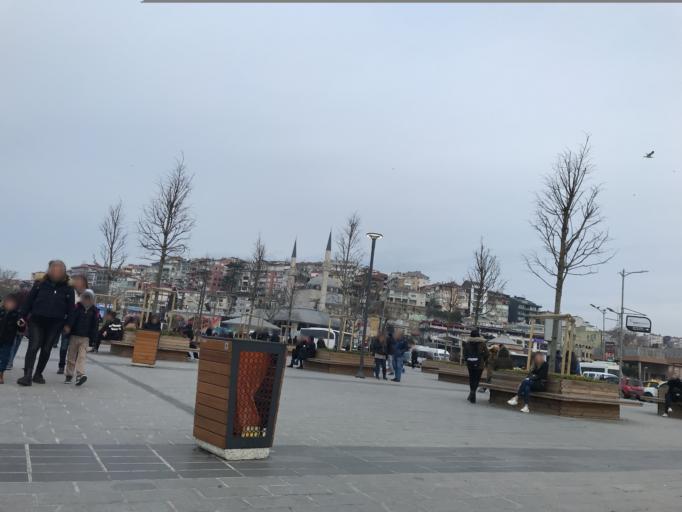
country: TR
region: Istanbul
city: UEskuedar
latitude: 41.0263
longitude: 29.0136
